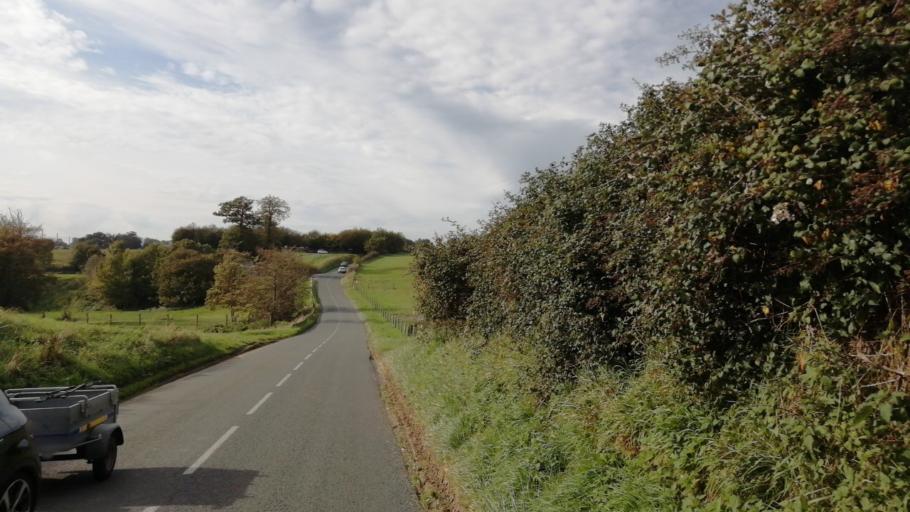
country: FR
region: Haute-Normandie
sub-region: Departement de la Seine-Maritime
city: Saint-Martin-du-Manoir
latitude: 49.5364
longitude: 0.2279
